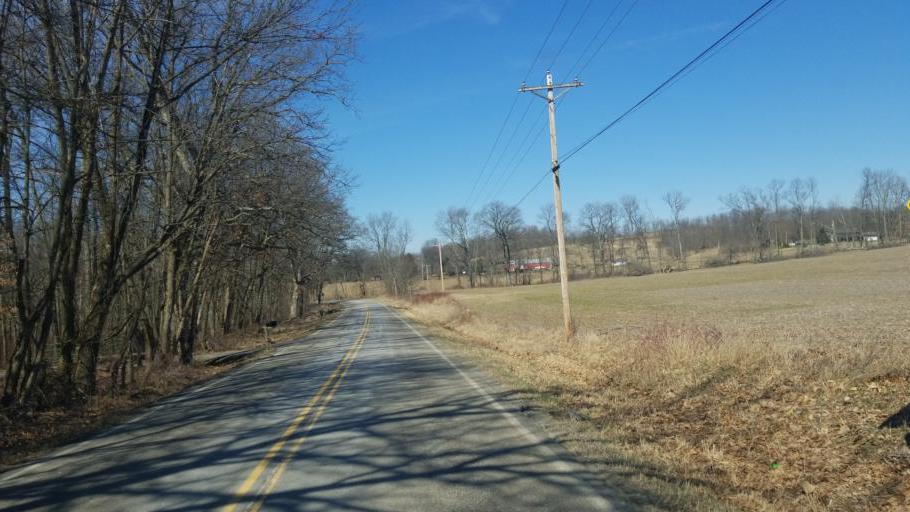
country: US
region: Ohio
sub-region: Knox County
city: Oak Hill
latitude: 40.4523
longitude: -82.1292
